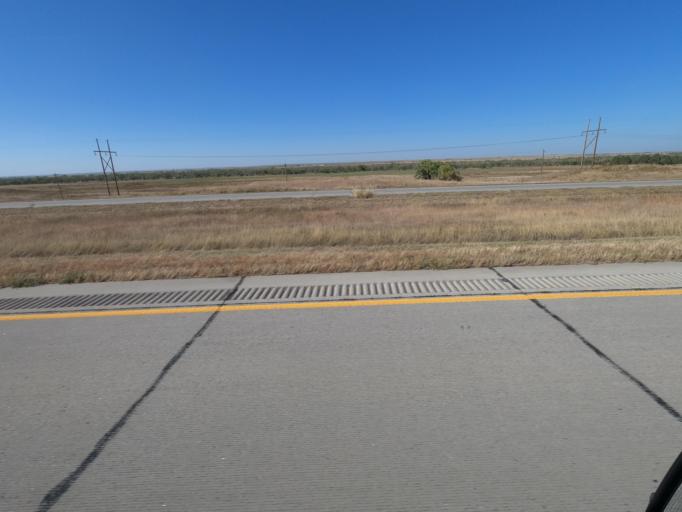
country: US
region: Colorado
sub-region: Sedgwick County
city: Julesburg
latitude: 40.9436
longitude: -102.2899
